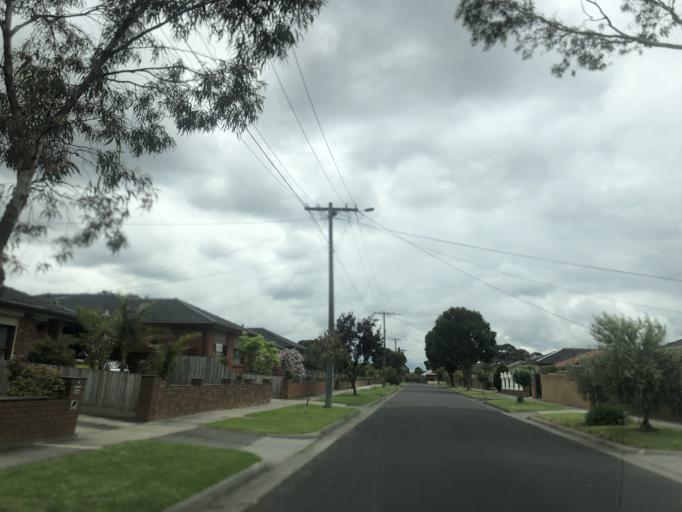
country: AU
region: Victoria
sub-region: Greater Dandenong
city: Dandenong North
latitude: -37.9726
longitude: 145.2086
